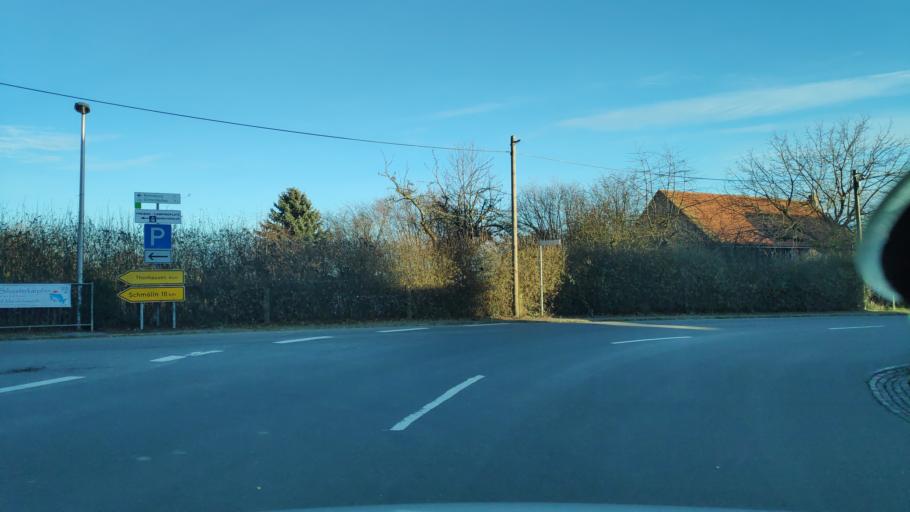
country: DE
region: Thuringia
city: Thonhausen
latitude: 50.8050
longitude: 12.3117
